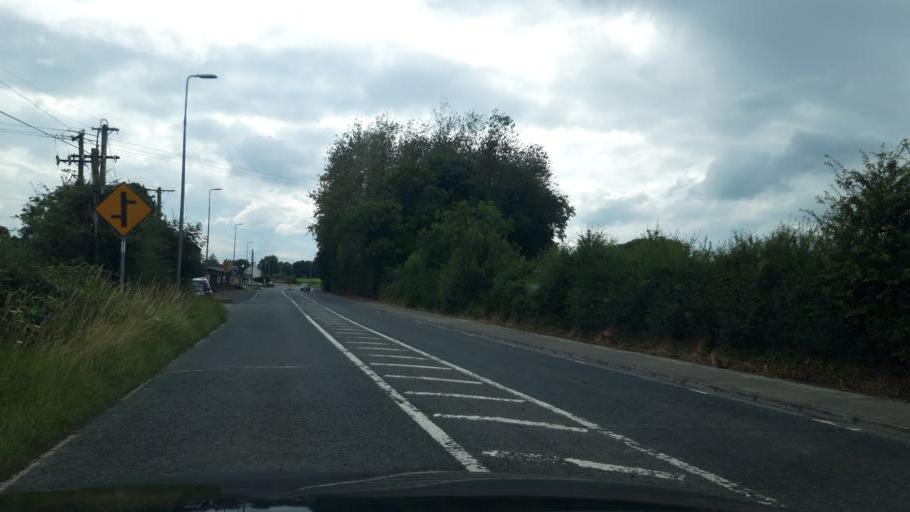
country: IE
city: Ballylinan
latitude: 52.8643
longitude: -7.1059
